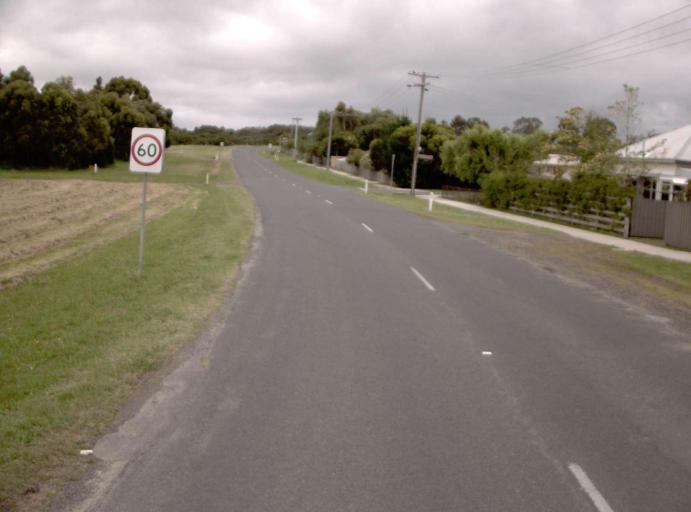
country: AU
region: Victoria
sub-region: Bass Coast
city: North Wonthaggi
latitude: -38.5957
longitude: 145.6063
